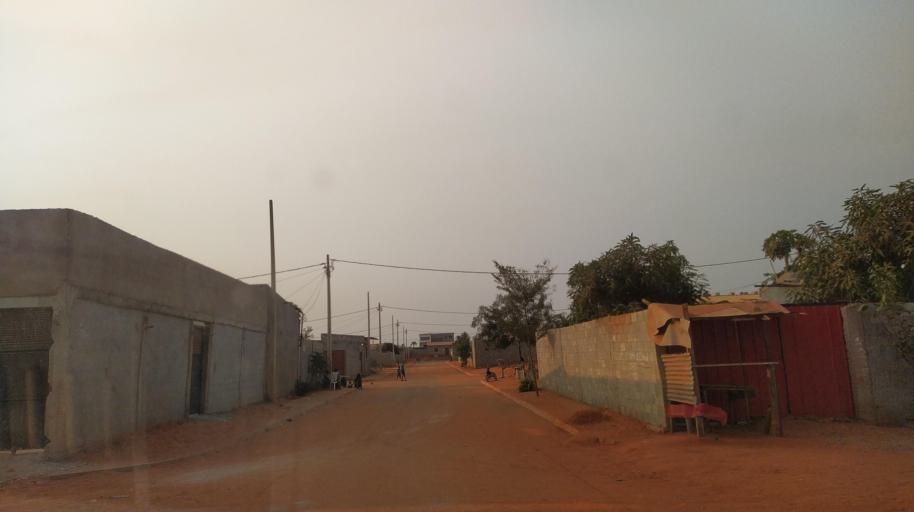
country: AO
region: Luanda
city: Luanda
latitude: -9.0727
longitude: 13.4266
